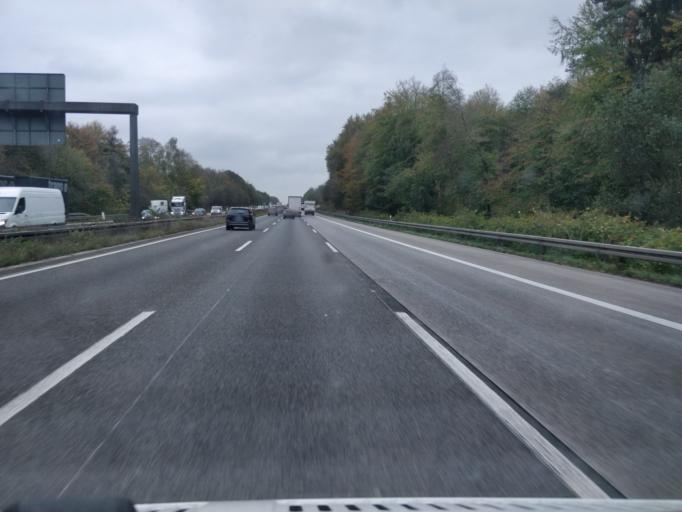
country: DE
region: North Rhine-Westphalia
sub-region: Regierungsbezirk Dusseldorf
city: Ratingen
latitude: 51.3386
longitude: 6.8738
